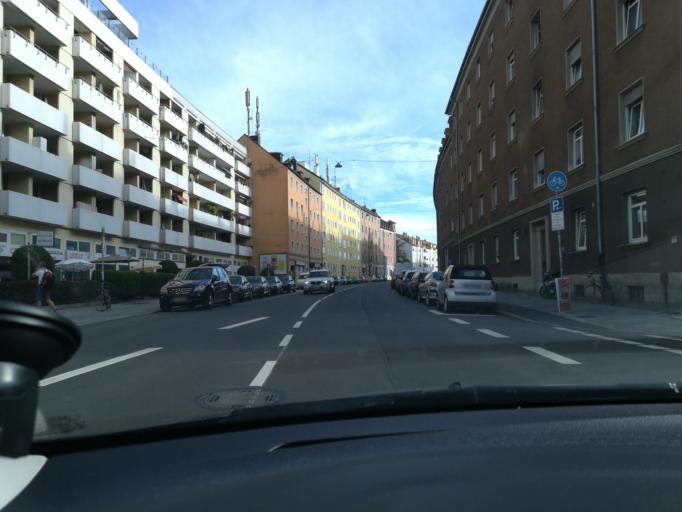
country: DE
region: Bavaria
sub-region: Upper Bavaria
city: Munich
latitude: 48.1247
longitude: 11.5411
